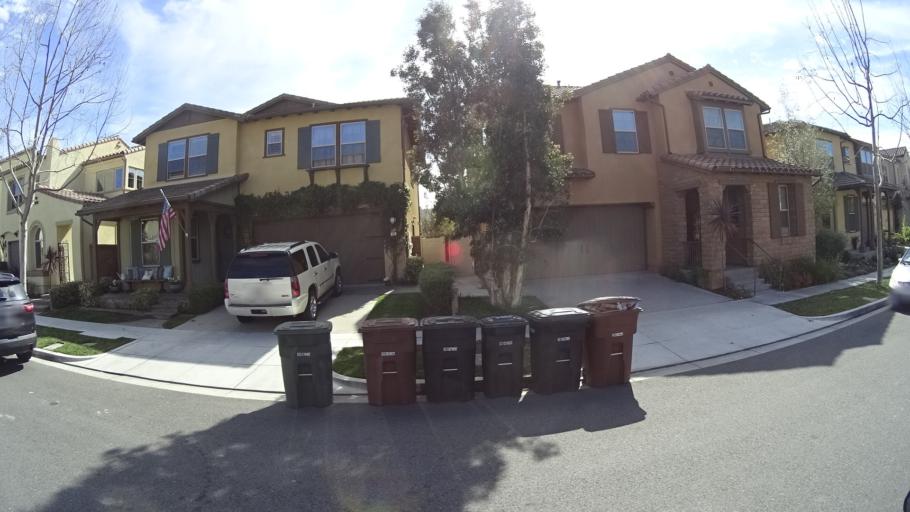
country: US
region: California
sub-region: Orange County
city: Ladera Ranch
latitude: 33.5268
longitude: -117.6213
